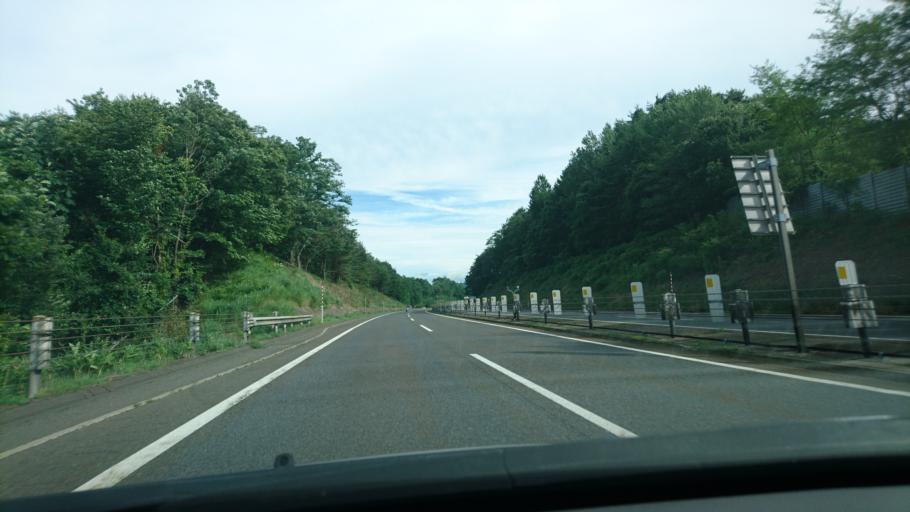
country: JP
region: Iwate
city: Shizukuishi
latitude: 39.9657
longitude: 141.0298
